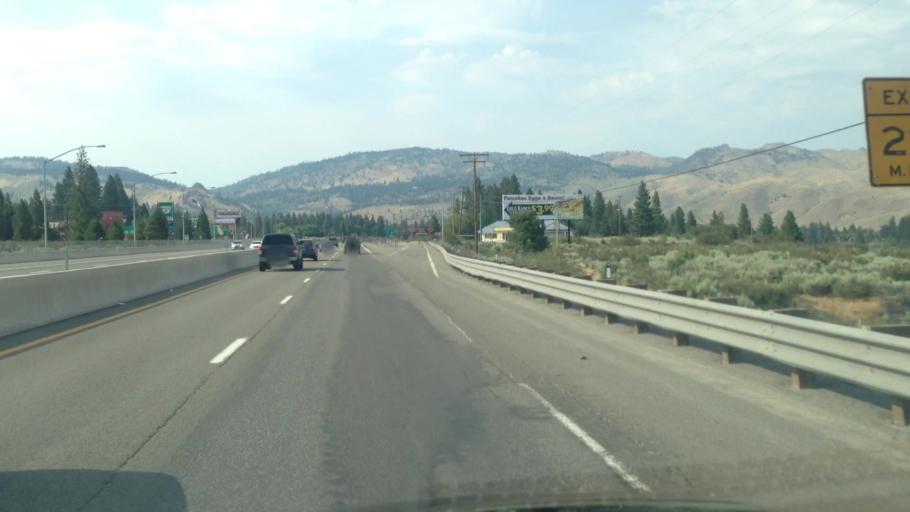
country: US
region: Nevada
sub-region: Washoe County
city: Verdi
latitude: 39.4992
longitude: -119.9984
